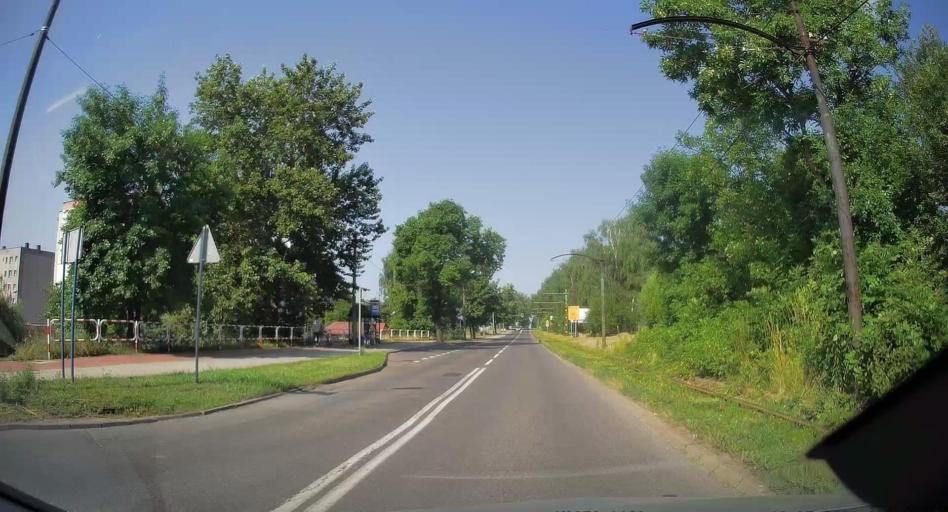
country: PL
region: Silesian Voivodeship
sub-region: Ruda Slaska
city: Ruda Slaska
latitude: 50.2716
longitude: 18.8815
